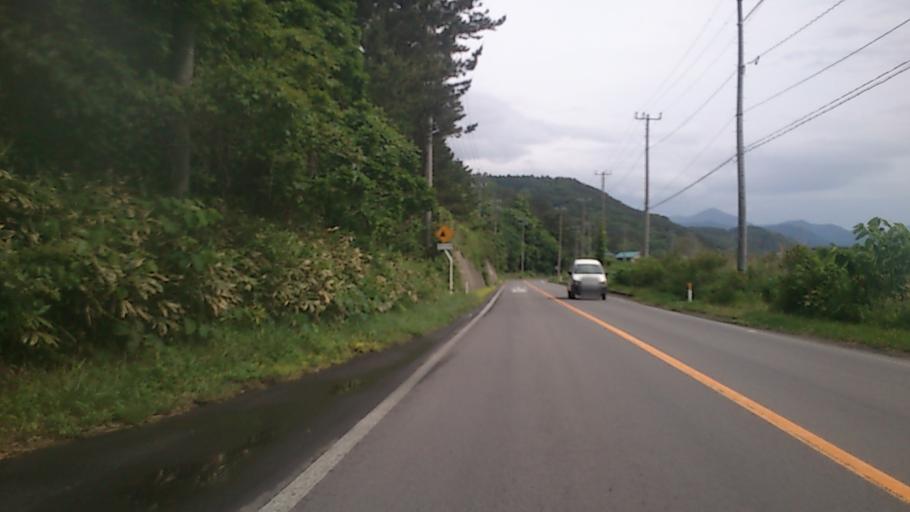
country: JP
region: Akita
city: Noshiromachi
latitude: 40.5497
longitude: 139.9436
